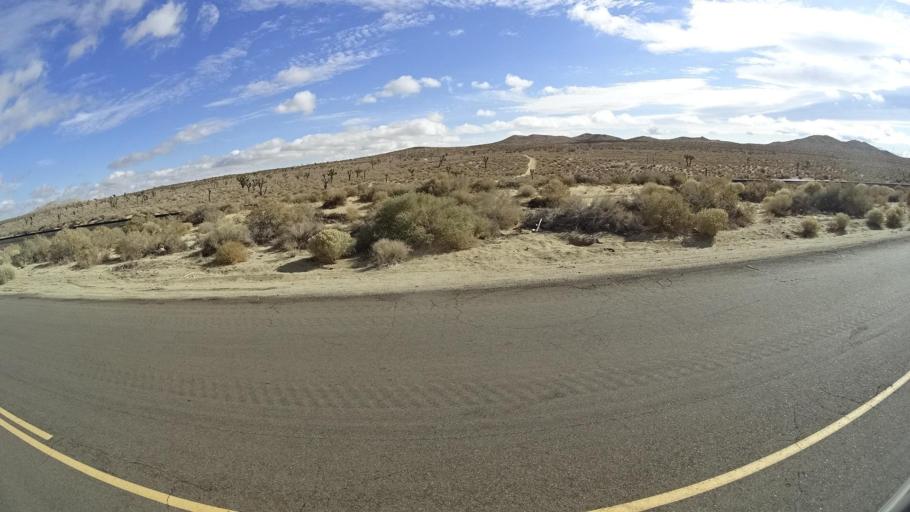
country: US
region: California
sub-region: Kern County
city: Rosamond
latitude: 34.9016
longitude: -118.1571
